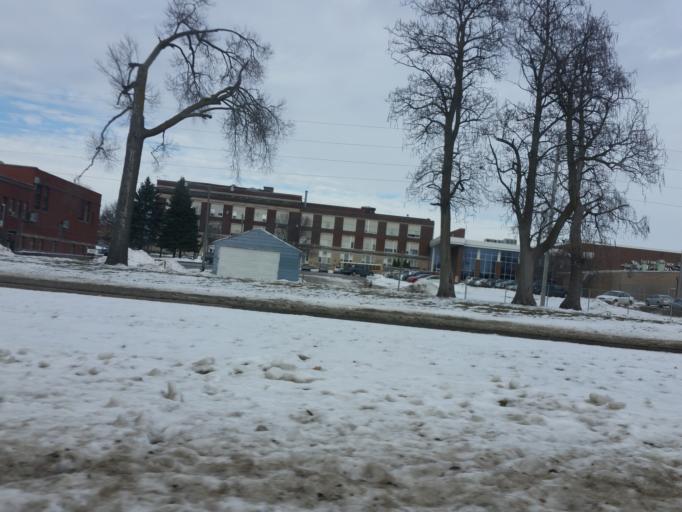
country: US
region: Iowa
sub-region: Black Hawk County
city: Waterloo
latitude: 42.5001
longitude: -92.3291
